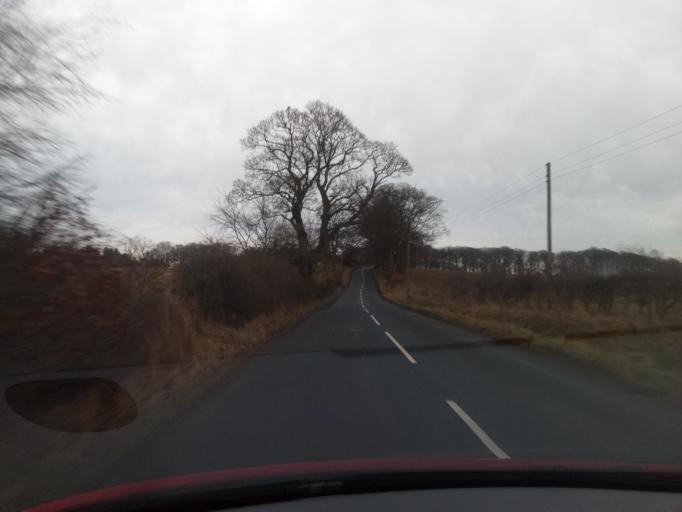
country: GB
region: England
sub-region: Northumberland
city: Whittingham
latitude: 55.4719
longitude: -1.8484
